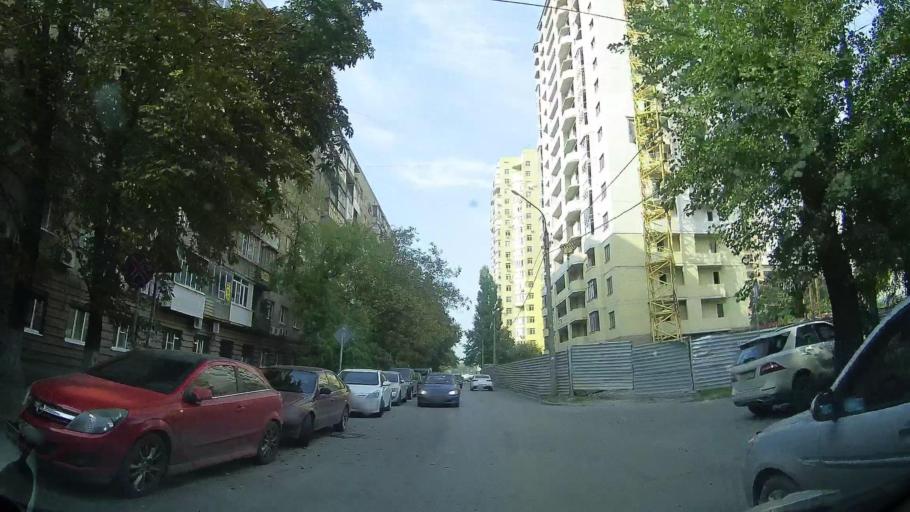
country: RU
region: Rostov
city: Rostov-na-Donu
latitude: 47.2329
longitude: 39.7245
